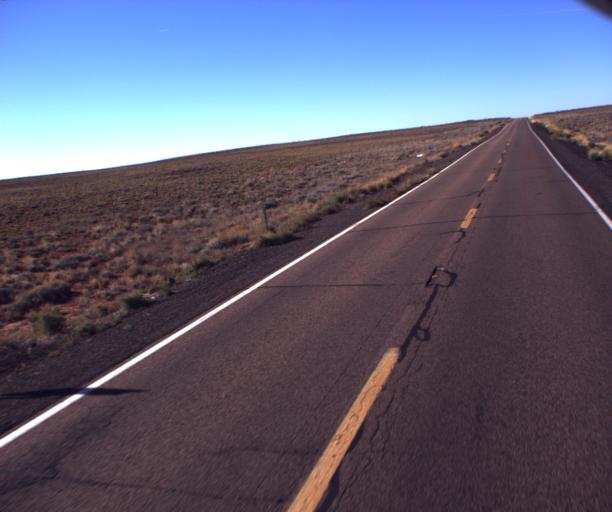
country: US
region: Arizona
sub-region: Navajo County
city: Holbrook
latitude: 34.8416
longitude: -110.1804
